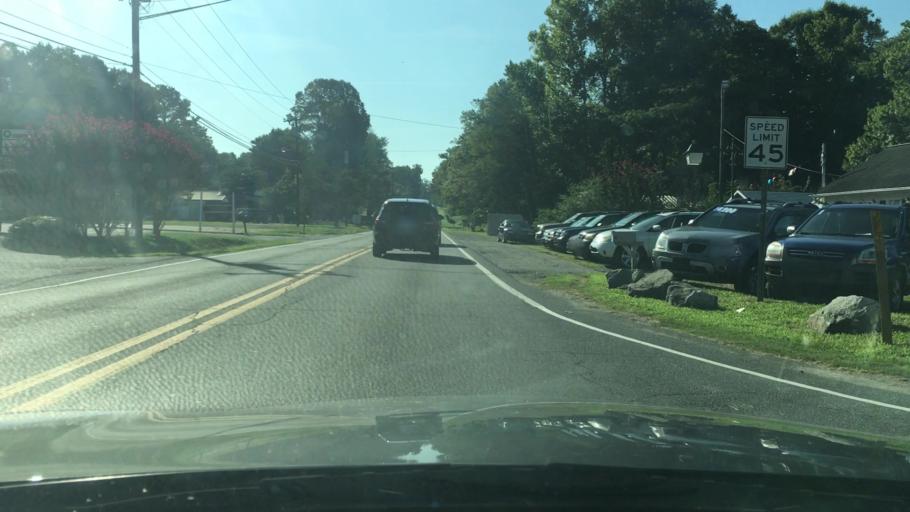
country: US
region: North Carolina
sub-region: Alamance County
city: Burlington
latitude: 36.0748
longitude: -79.4441
